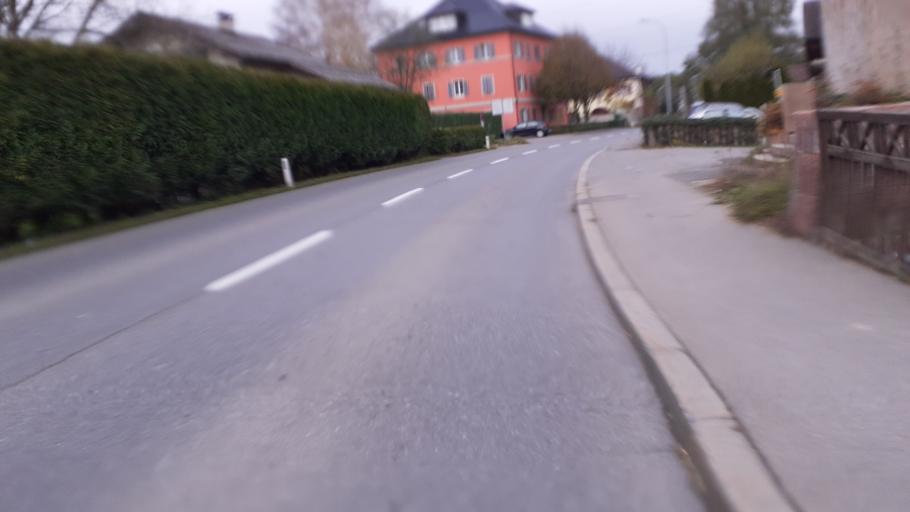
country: AT
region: Vorarlberg
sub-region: Politischer Bezirk Feldkirch
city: Meiningen
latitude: 47.3020
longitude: 9.5754
